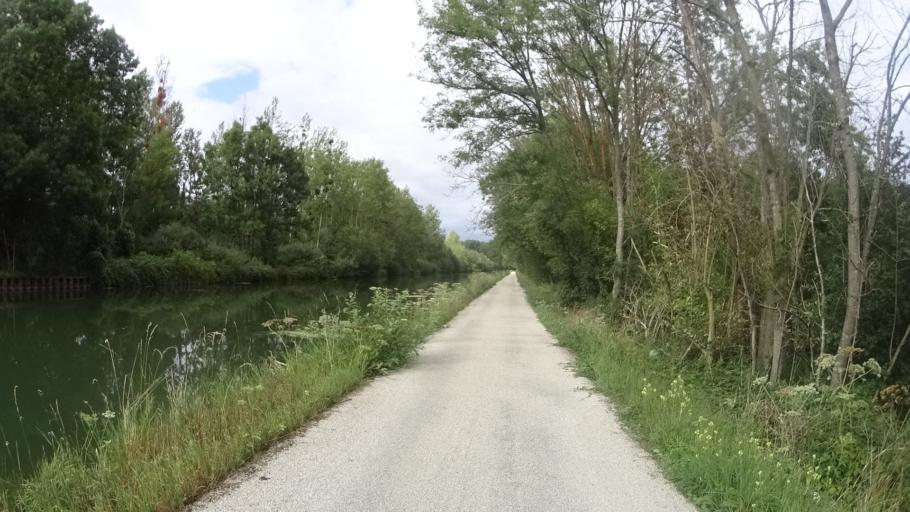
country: FR
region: Picardie
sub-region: Departement de l'Aisne
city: Itancourt
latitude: 49.7699
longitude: 3.3904
